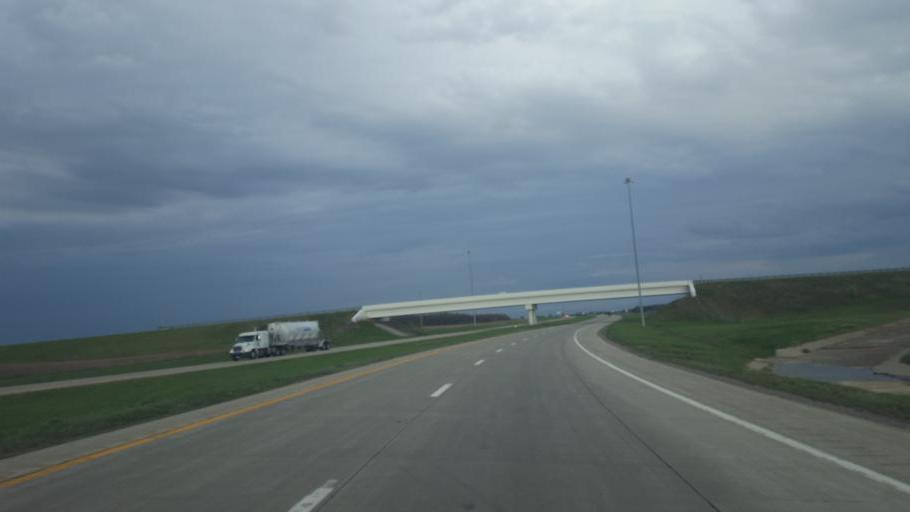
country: US
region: Ohio
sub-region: Wyandot County
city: Upper Sandusky
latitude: 40.8090
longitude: -83.2246
